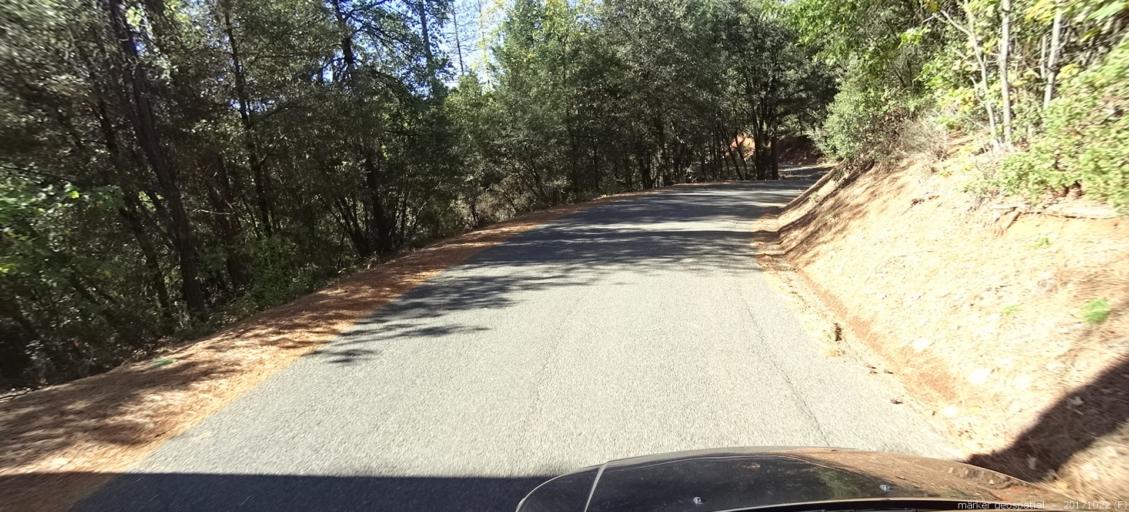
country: US
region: California
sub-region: Shasta County
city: Central Valley (historical)
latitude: 40.9428
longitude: -122.4406
